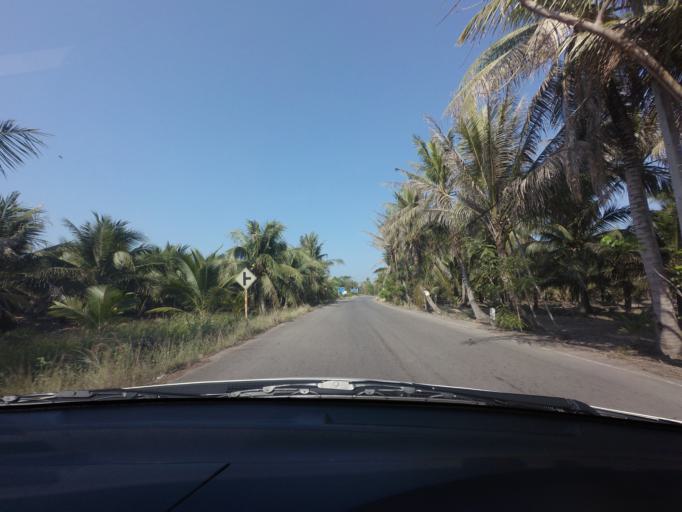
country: TH
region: Ratchaburi
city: Damnoen Saduak
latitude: 13.4890
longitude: 100.0206
